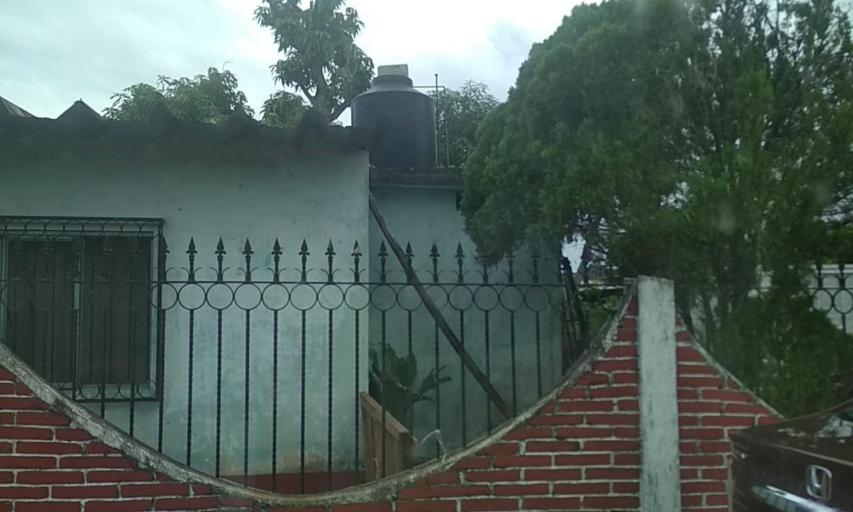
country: MX
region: Veracruz
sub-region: Martinez de la Torre
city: El Progreso
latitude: 20.0957
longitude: -97.0131
